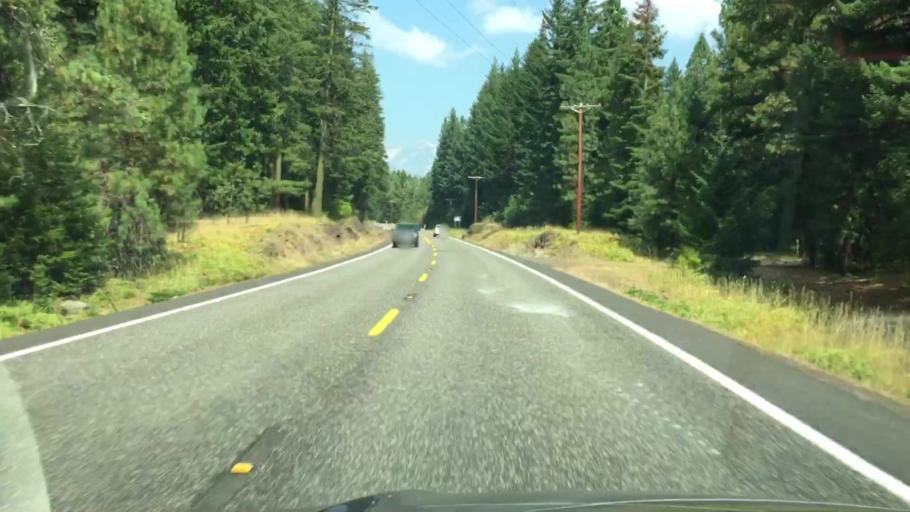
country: US
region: Washington
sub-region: Klickitat County
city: White Salmon
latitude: 45.9588
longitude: -121.4893
